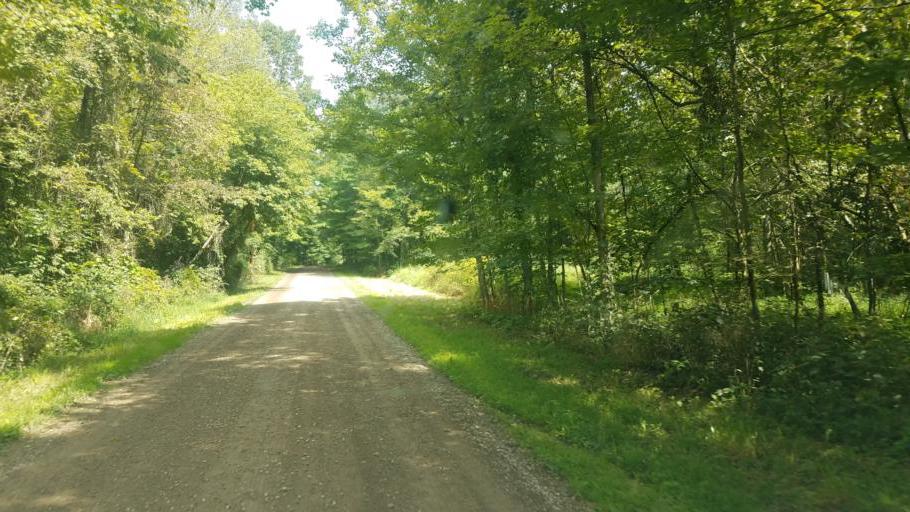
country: US
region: Ohio
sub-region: Licking County
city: Utica
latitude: 40.2384
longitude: -82.4824
